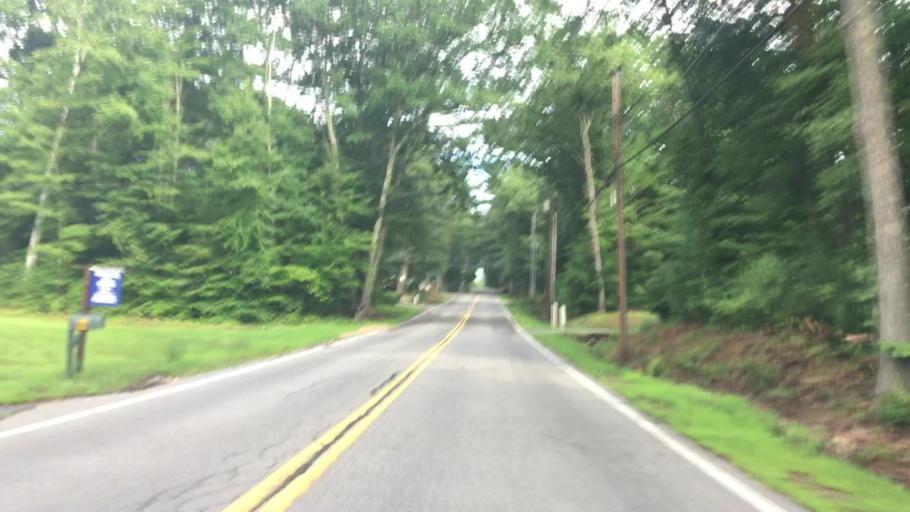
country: US
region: New Hampshire
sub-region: Strafford County
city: Rochester
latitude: 43.3564
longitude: -70.9899
